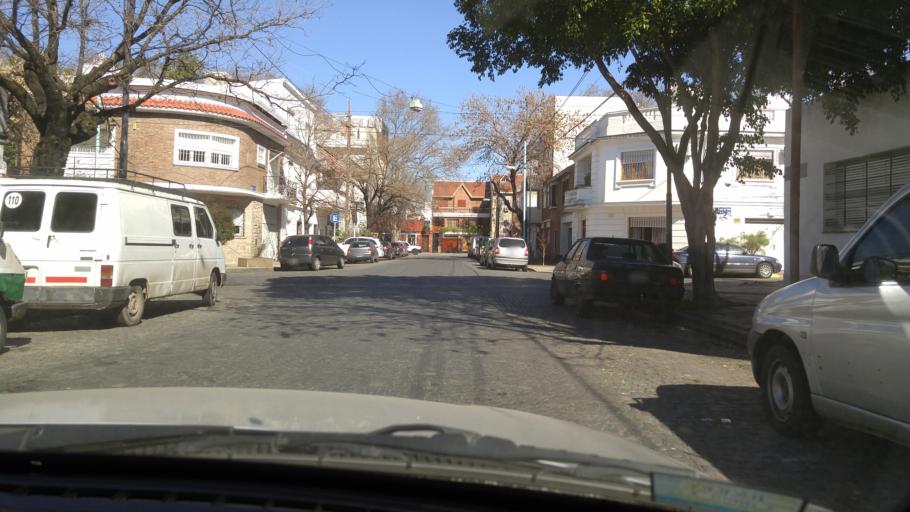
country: AR
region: Buenos Aires F.D.
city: Villa Santa Rita
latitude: -34.6245
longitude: -58.4873
